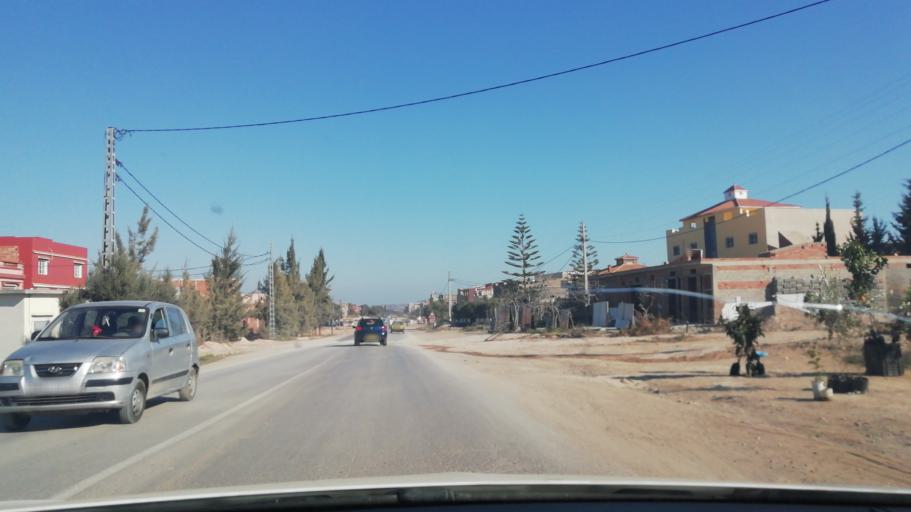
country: DZ
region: Tlemcen
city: Nedroma
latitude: 35.0127
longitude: -1.8991
